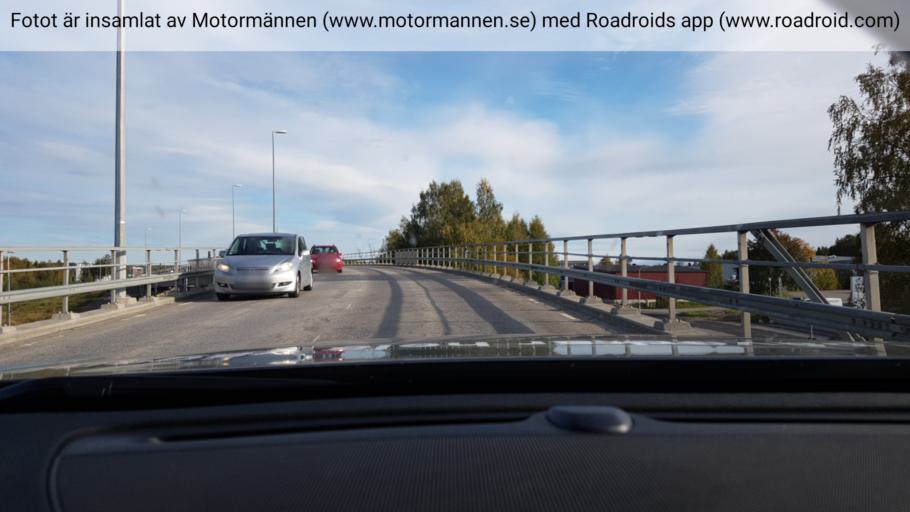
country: SE
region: Norrbotten
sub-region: Lulea Kommun
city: Bergnaset
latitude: 65.6140
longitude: 22.1084
